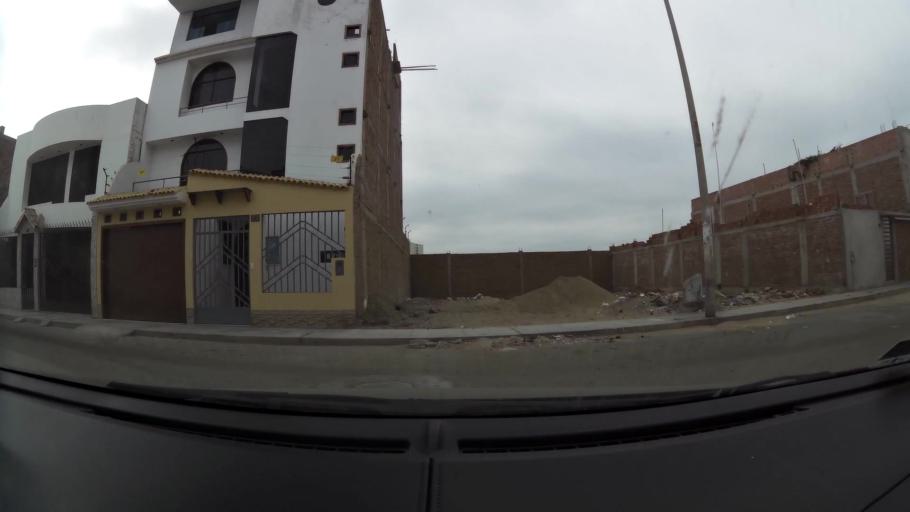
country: PE
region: La Libertad
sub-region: Provincia de Trujillo
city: La Esperanza
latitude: -8.0964
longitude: -79.0469
